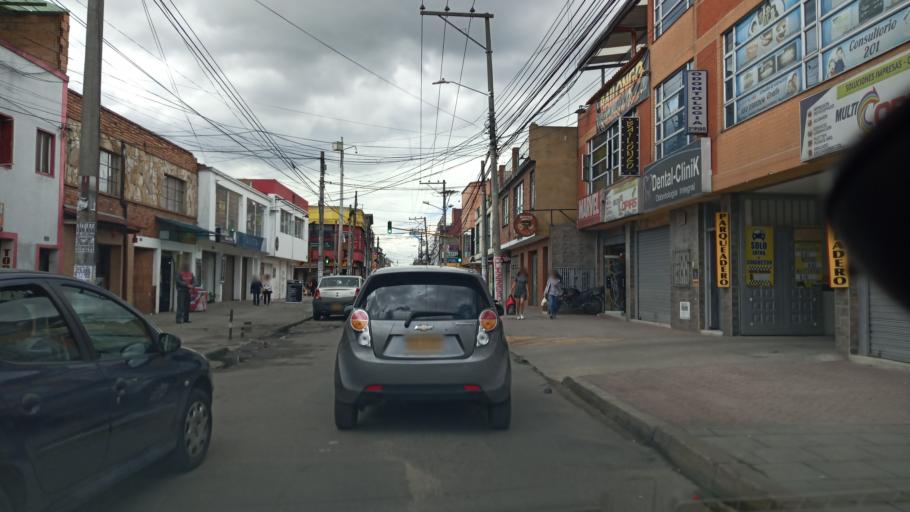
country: CO
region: Cundinamarca
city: Funza
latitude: 4.6734
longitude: -74.1429
